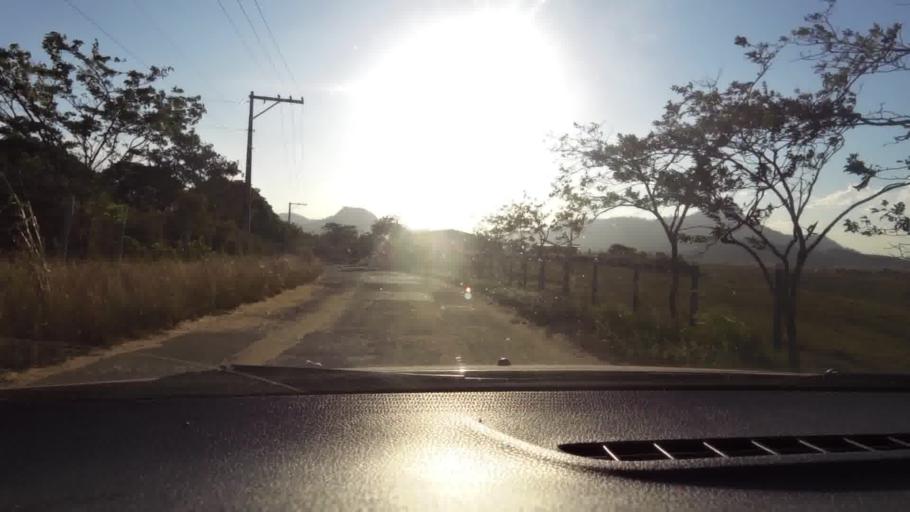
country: BR
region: Espirito Santo
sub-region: Guarapari
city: Guarapari
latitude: -20.5310
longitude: -40.4589
